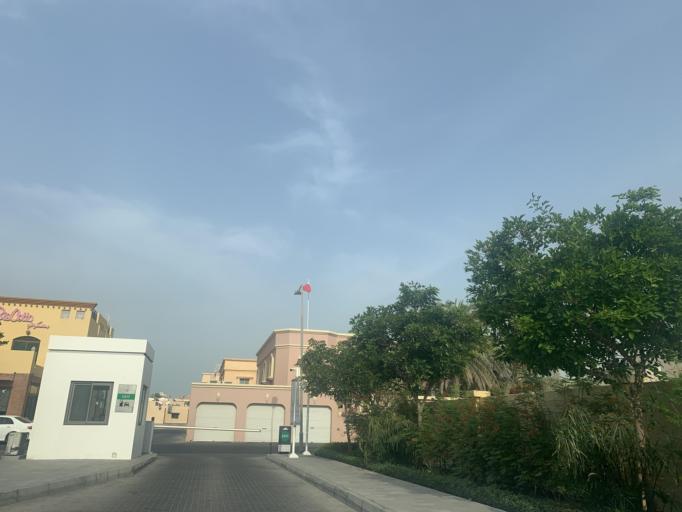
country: BH
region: Northern
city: Ar Rifa'
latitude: 26.1339
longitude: 50.5491
